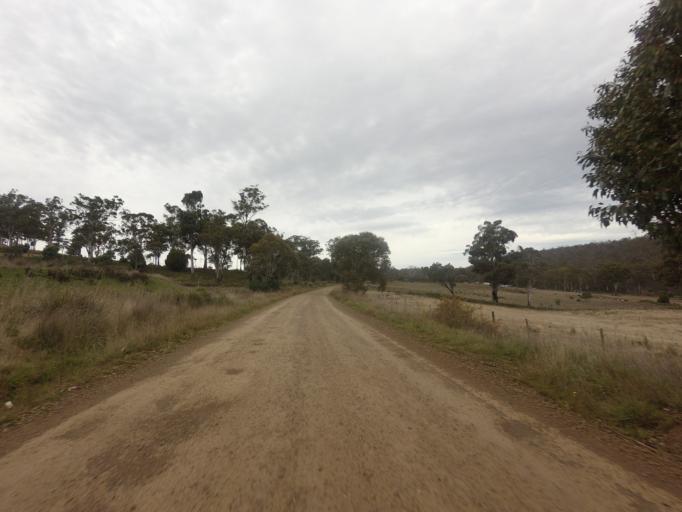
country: AU
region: Tasmania
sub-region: Derwent Valley
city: New Norfolk
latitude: -42.5612
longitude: 146.9531
